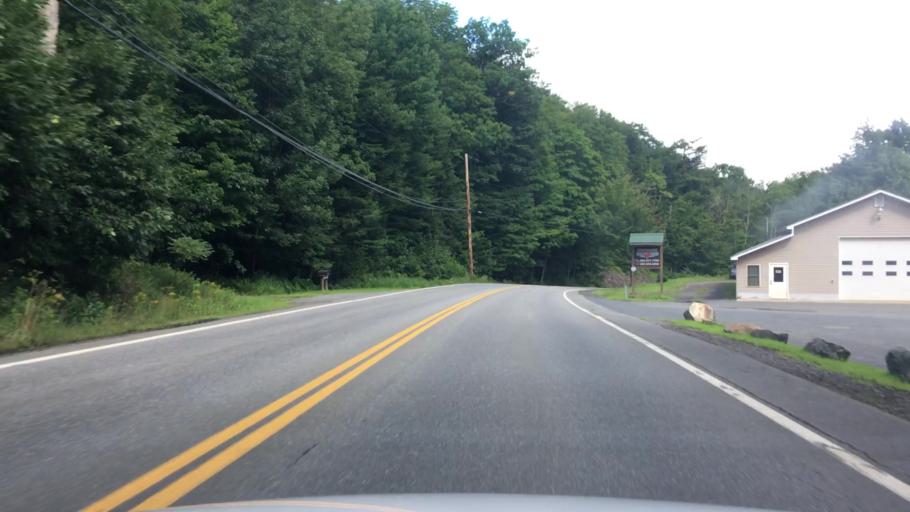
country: US
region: Vermont
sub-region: Windham County
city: West Brattleboro
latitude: 42.8778
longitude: -72.6828
